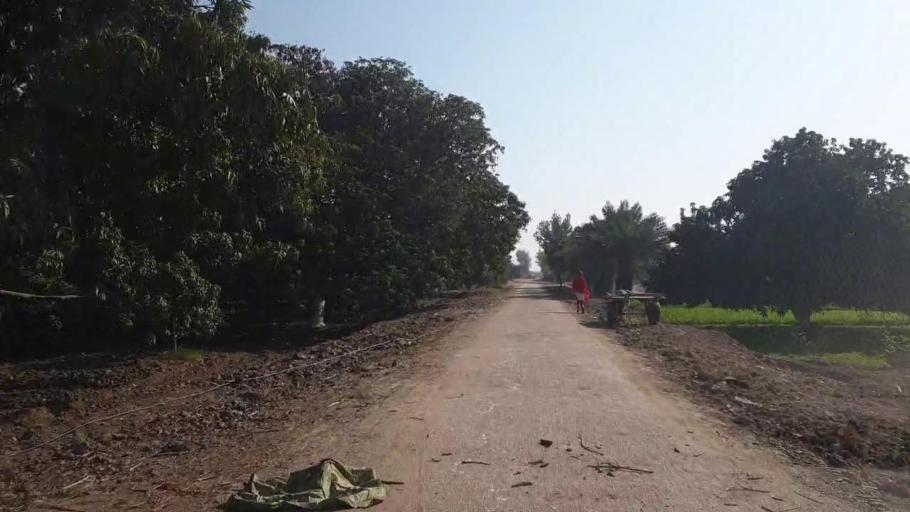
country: PK
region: Sindh
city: Tando Allahyar
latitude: 25.3670
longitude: 68.6660
